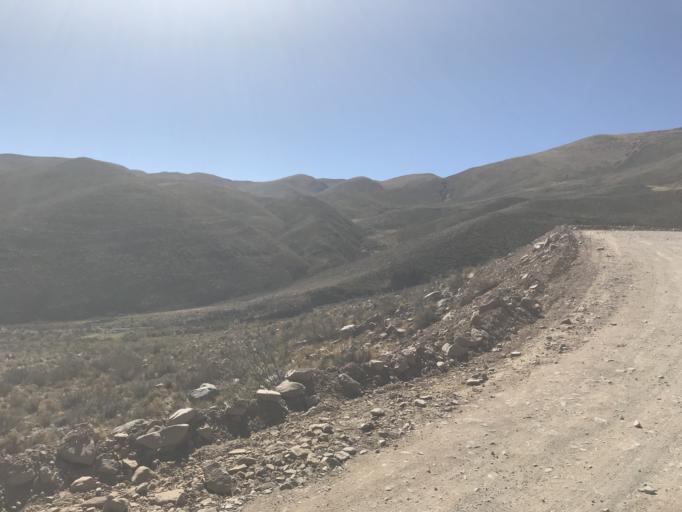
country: AR
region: Jujuy
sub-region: Departamento de Humahuaca
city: Humahuaca
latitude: -23.1950
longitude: -65.2205
